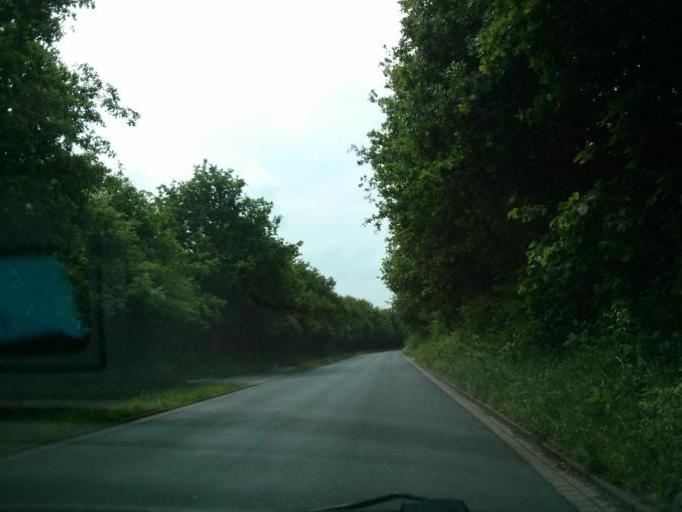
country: DE
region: Lower Saxony
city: Loxstedt
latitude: 53.4841
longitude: 8.6640
